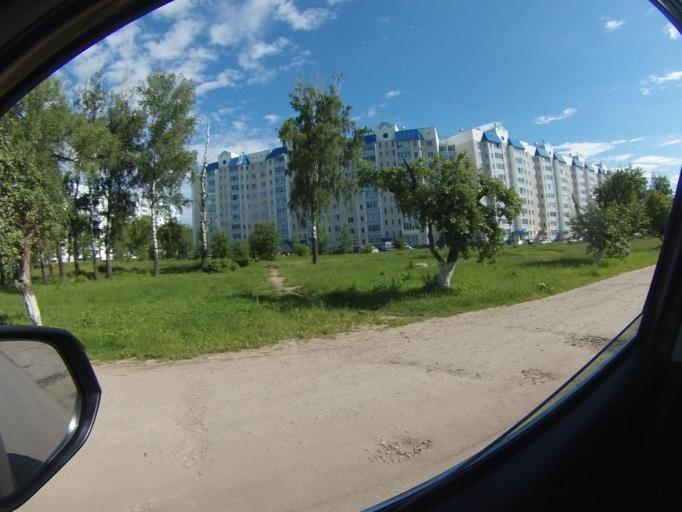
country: RU
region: Orjol
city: Mtsensk
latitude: 53.2923
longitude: 36.6009
